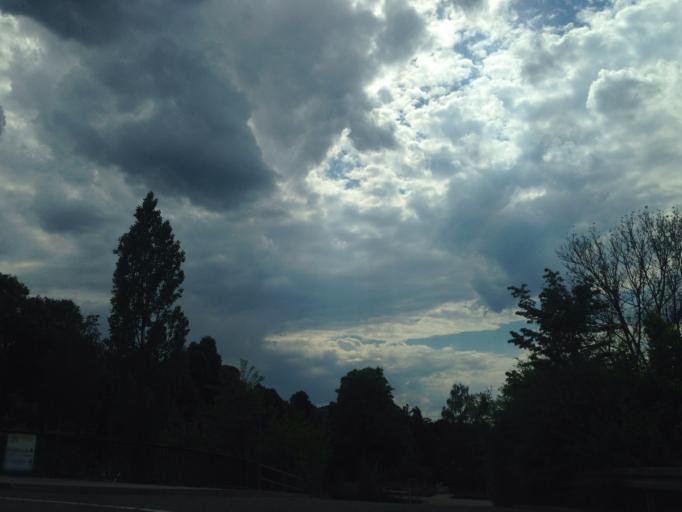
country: DE
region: Thuringia
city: Possneck
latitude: 50.6943
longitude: 11.6003
